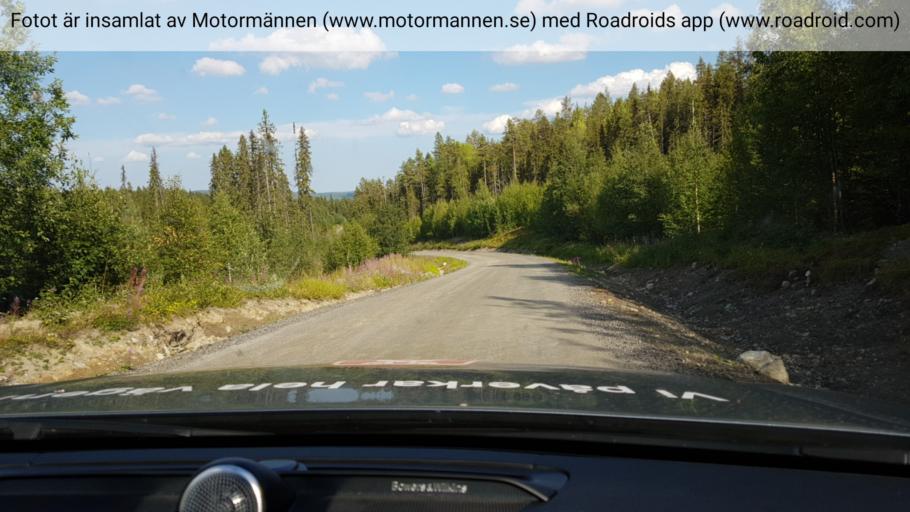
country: SE
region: Vaesterbotten
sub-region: Dorotea Kommun
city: Dorotea
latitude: 63.9215
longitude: 16.2304
